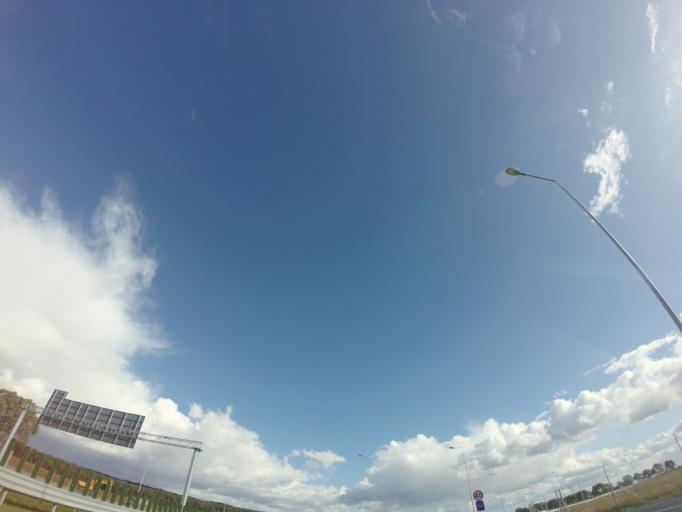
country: PL
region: Lower Silesian Voivodeship
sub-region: Powiat polkowicki
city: Radwanice
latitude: 51.6002
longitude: 15.9634
